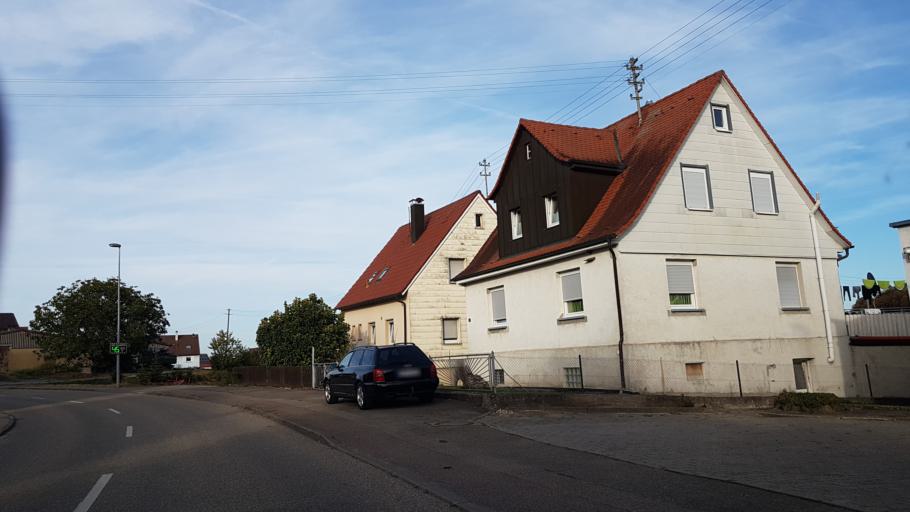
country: DE
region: Baden-Wuerttemberg
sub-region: Regierungsbezirk Stuttgart
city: Neuenstadt am Kocher
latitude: 49.2120
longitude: 9.3522
